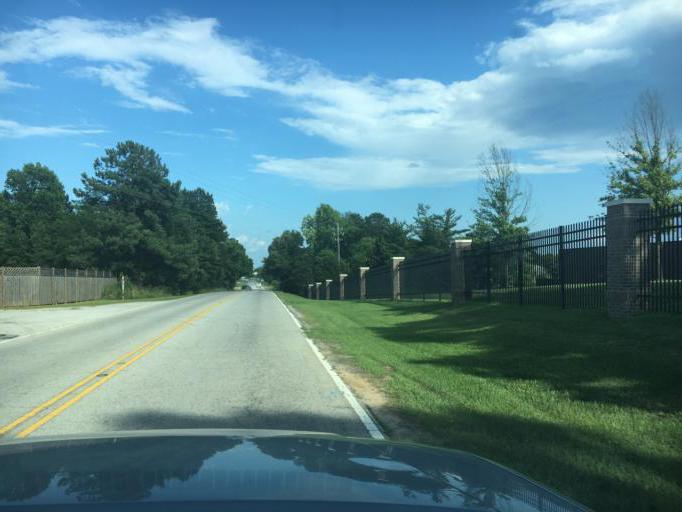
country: US
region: South Carolina
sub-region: Greenville County
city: Mauldin
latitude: 34.7969
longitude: -82.3112
